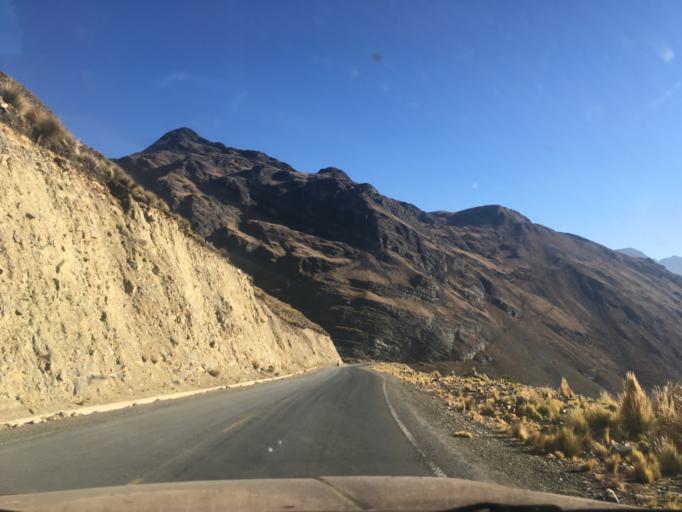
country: BO
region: La Paz
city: Quime
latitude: -17.0308
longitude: -67.2868
